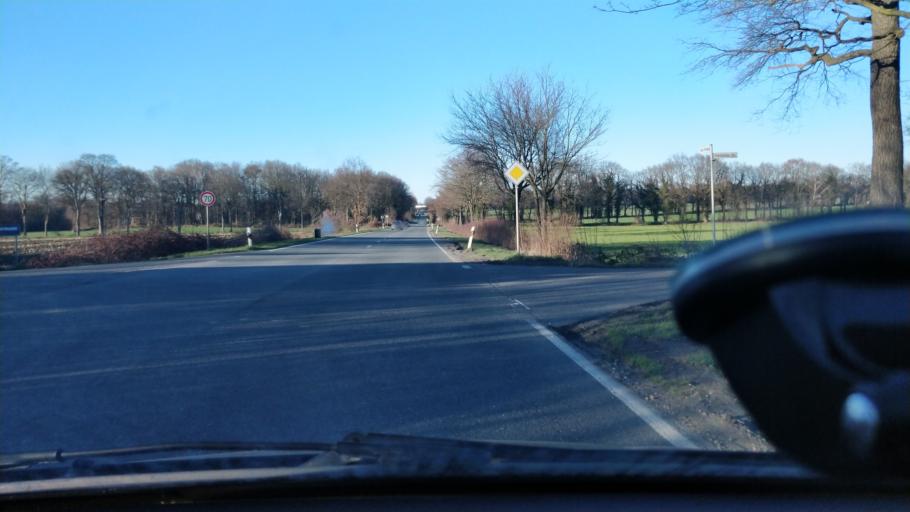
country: DE
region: North Rhine-Westphalia
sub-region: Regierungsbezirk Munster
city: Bottrop
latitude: 51.5931
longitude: 6.8875
